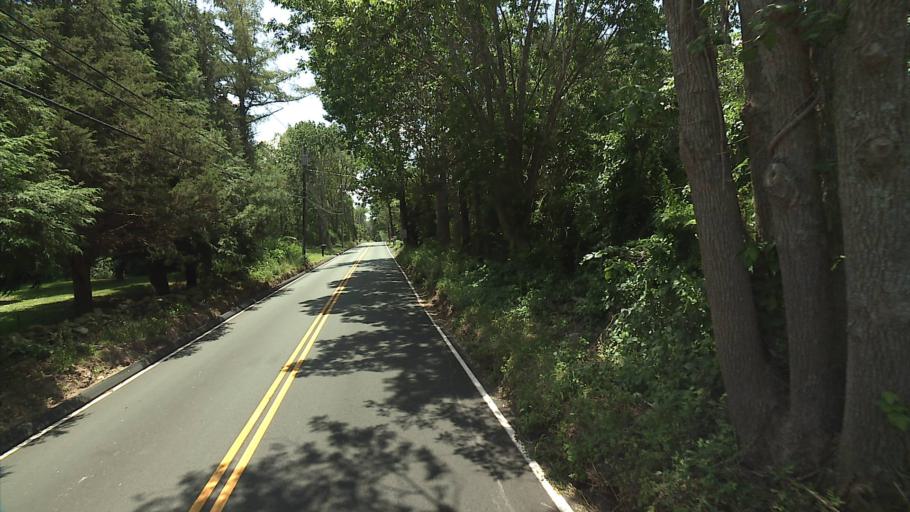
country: US
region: Connecticut
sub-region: New London County
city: Preston City
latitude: 41.5662
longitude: -71.8918
